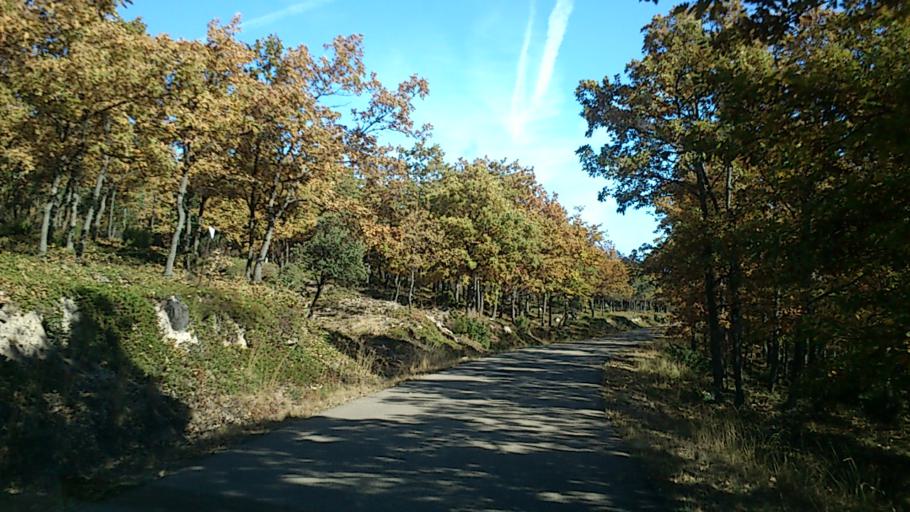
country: ES
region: Aragon
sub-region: Provincia de Zaragoza
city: Litago
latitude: 41.8003
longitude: -1.7890
